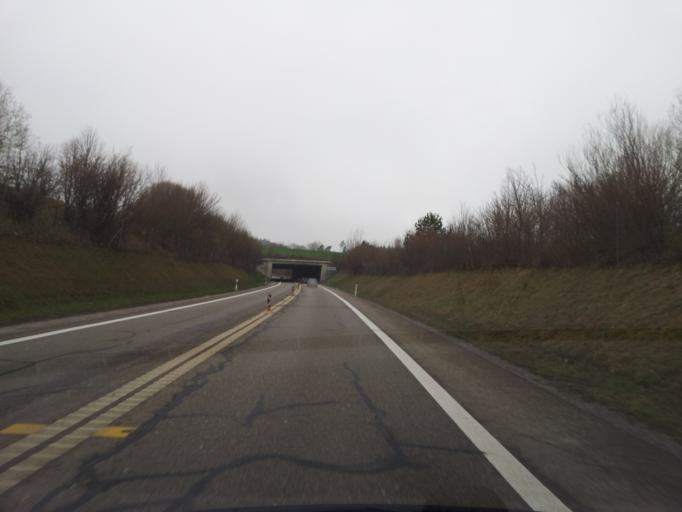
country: CH
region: Zurich
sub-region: Bezirk Winterthur
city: Hettlingen
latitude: 47.5438
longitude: 8.6906
